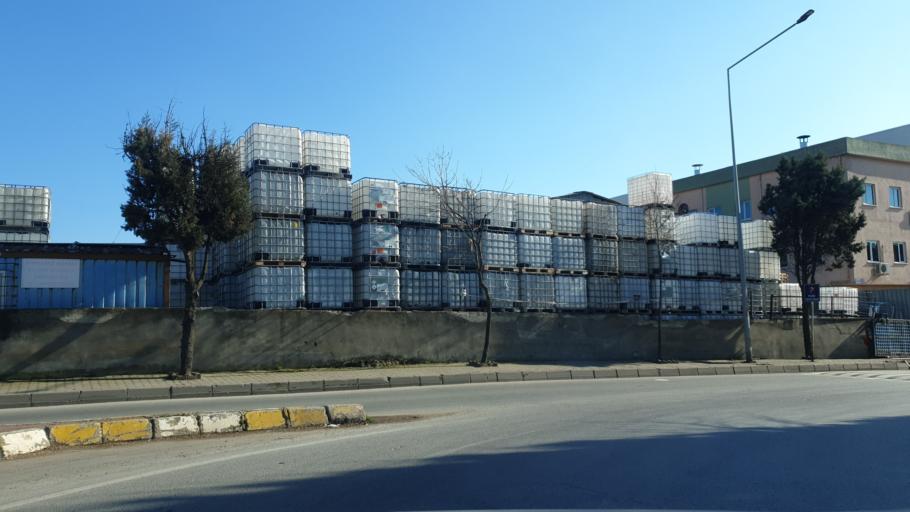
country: TR
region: Kocaeli
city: Balcik
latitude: 40.8806
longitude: 29.3709
